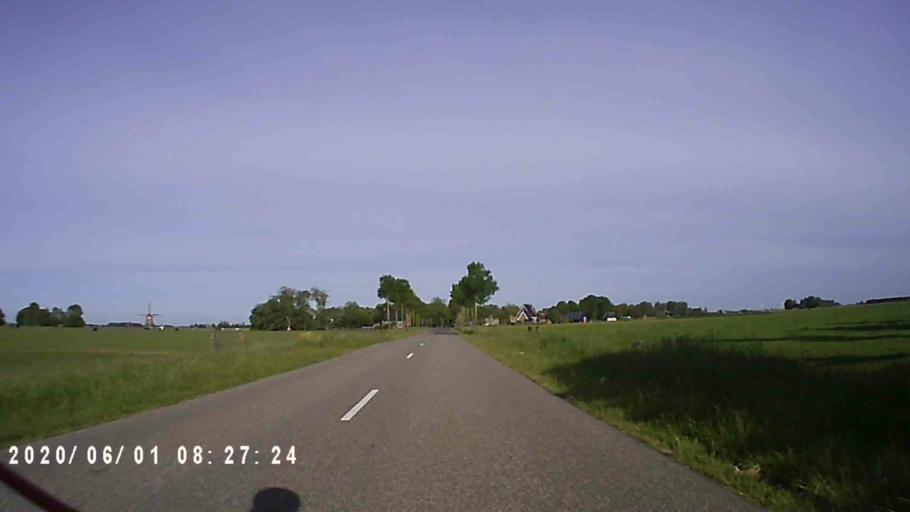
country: NL
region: Friesland
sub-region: Gemeente Ferwerderadiel
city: Burdaard
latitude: 53.3002
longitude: 5.8562
